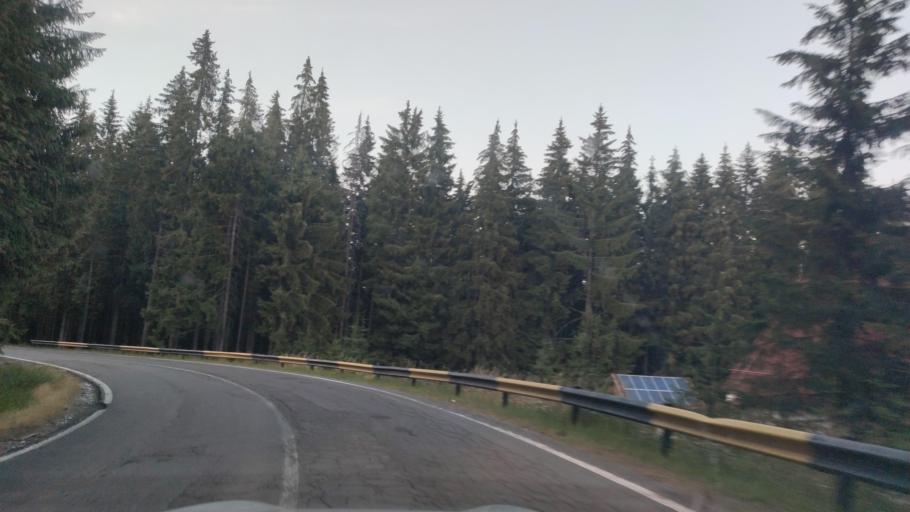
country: RO
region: Harghita
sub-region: Comuna Varsag
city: Varsag
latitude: 46.6615
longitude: 25.3040
